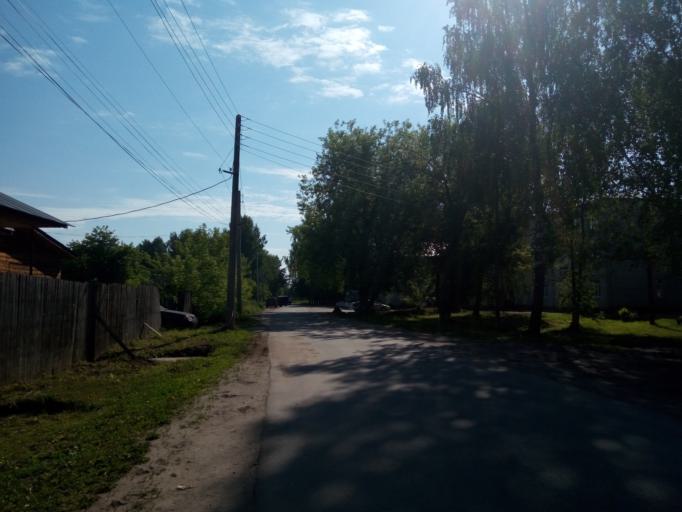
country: RU
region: Nizjnij Novgorod
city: Voskresenskoye
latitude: 56.8319
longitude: 45.4382
